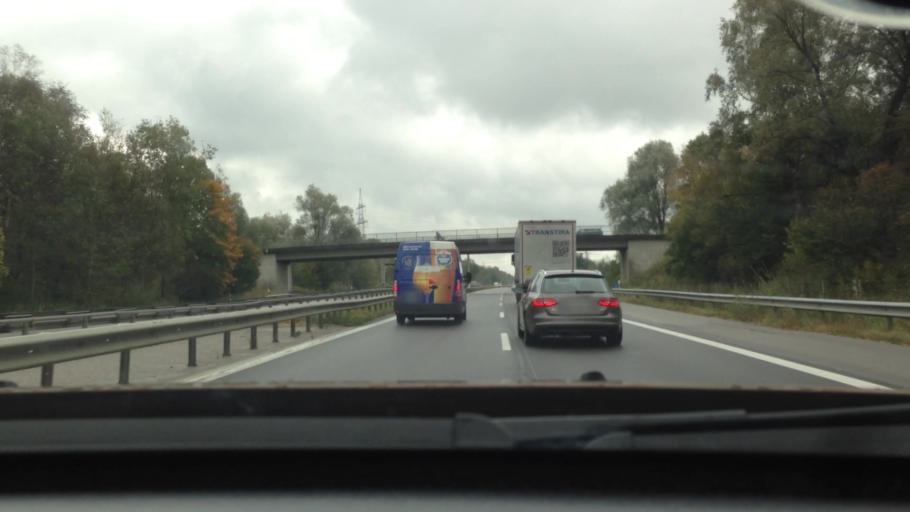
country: DE
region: Bavaria
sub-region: Upper Bavaria
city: Grobenzell
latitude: 48.2054
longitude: 11.3957
